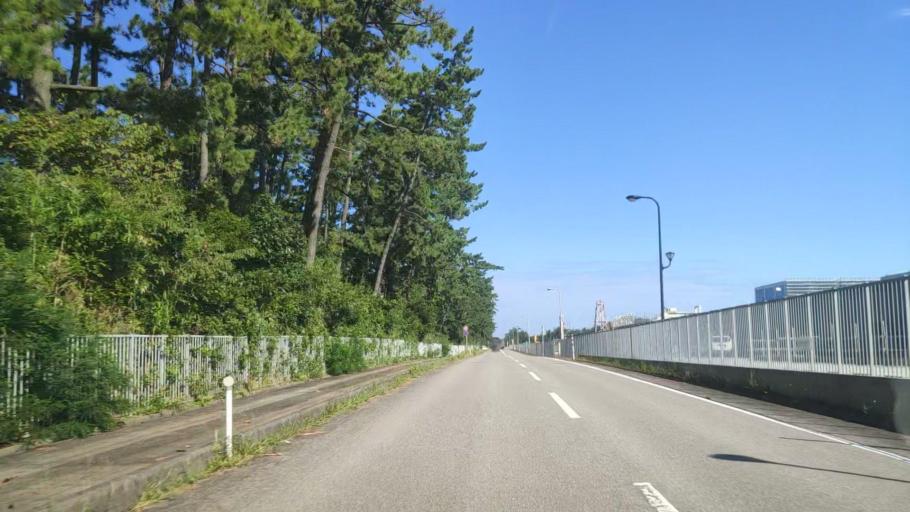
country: JP
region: Ishikawa
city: Hakui
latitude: 37.0579
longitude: 136.7239
